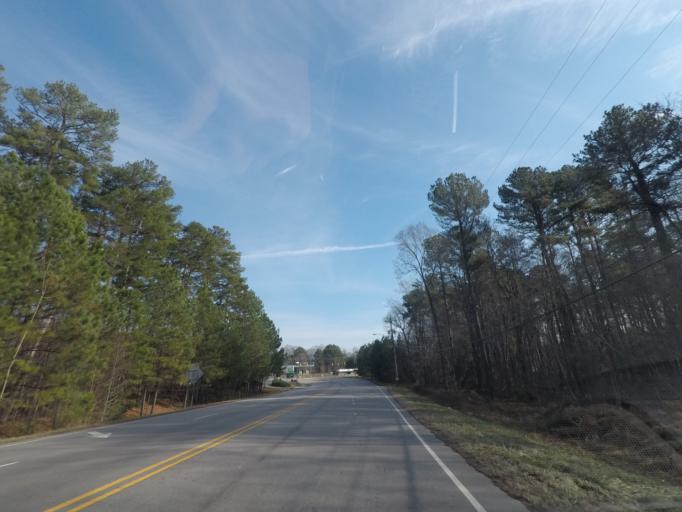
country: US
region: North Carolina
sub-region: Durham County
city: Durham
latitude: 36.0834
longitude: -78.9336
